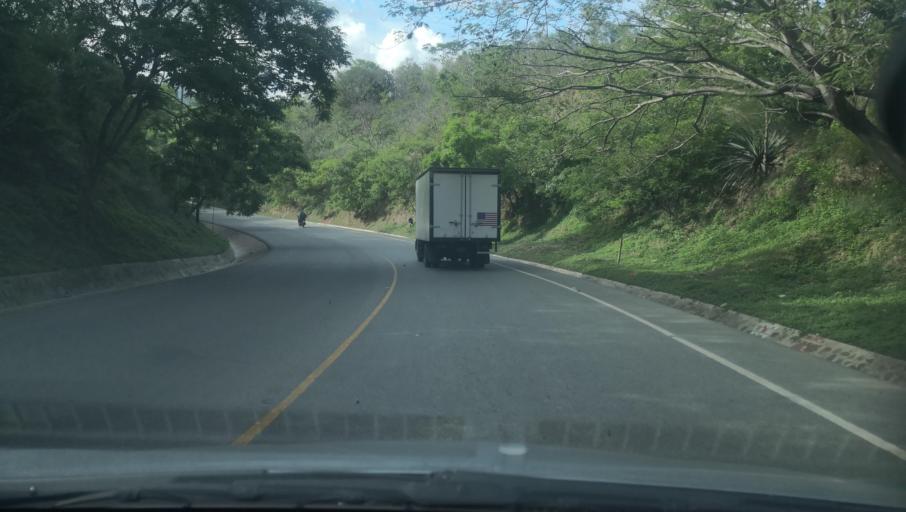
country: NI
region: Nueva Segovia
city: Ocotal
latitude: 13.6092
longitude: -86.4694
